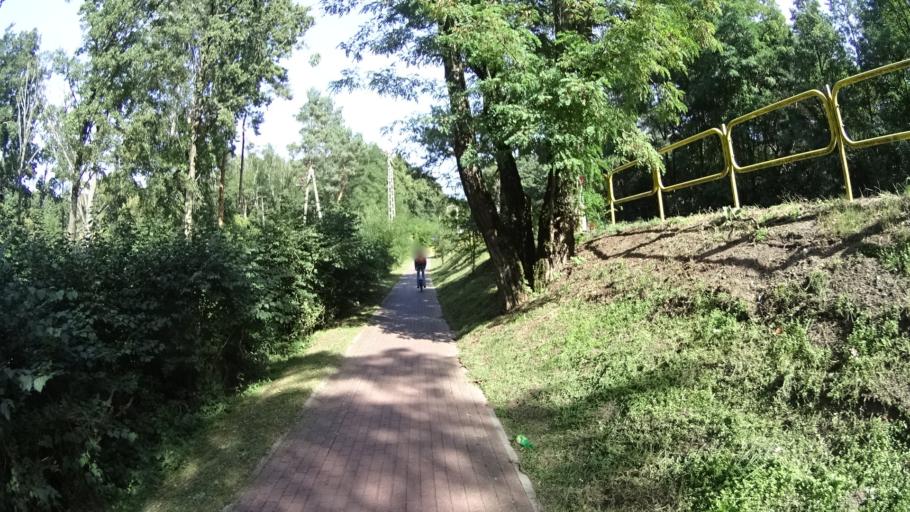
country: PL
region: Masovian Voivodeship
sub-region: Powiat legionowski
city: Bialobrzegi
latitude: 52.4405
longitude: 21.0495
